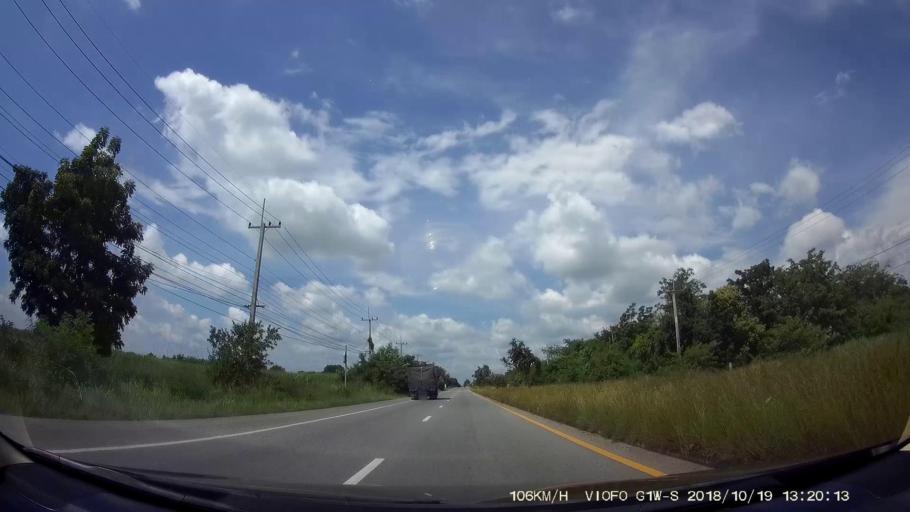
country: TH
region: Chaiyaphum
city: Chatturat
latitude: 15.4422
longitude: 101.8291
